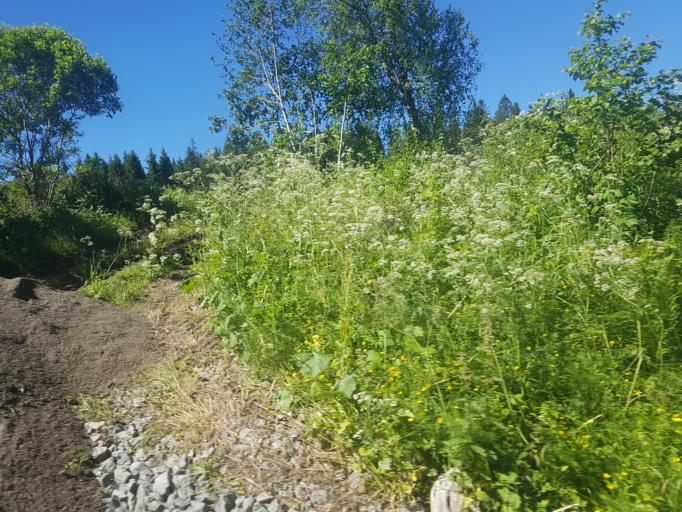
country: NO
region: Sor-Trondelag
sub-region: Skaun
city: Borsa
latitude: 63.4383
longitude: 10.1987
